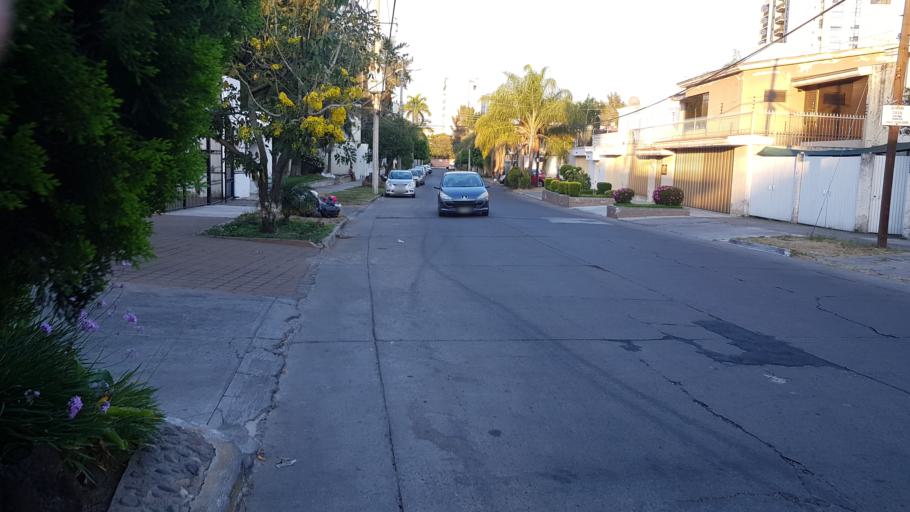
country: MX
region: Jalisco
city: Guadalajara
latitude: 20.6868
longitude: -103.4179
